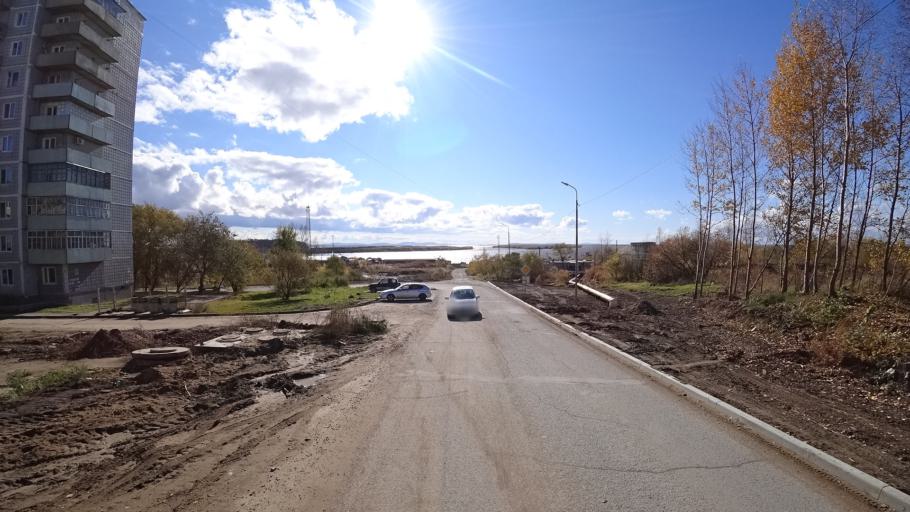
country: RU
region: Khabarovsk Krai
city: Amursk
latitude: 50.2154
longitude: 136.8922
